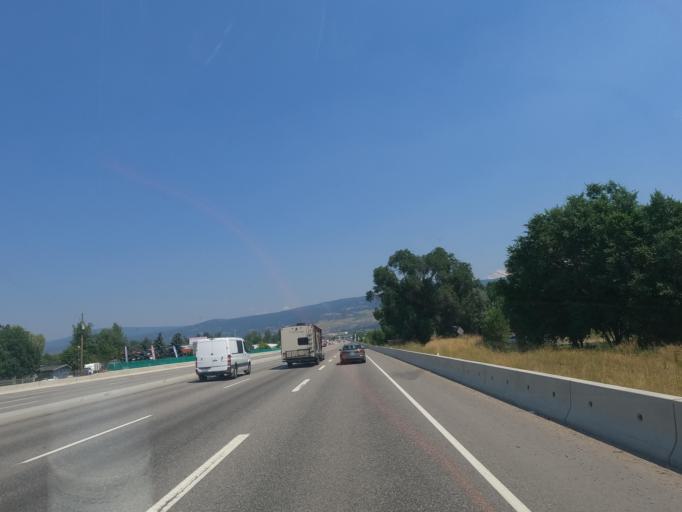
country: CA
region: British Columbia
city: Kelowna
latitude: 49.9122
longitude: -119.3971
